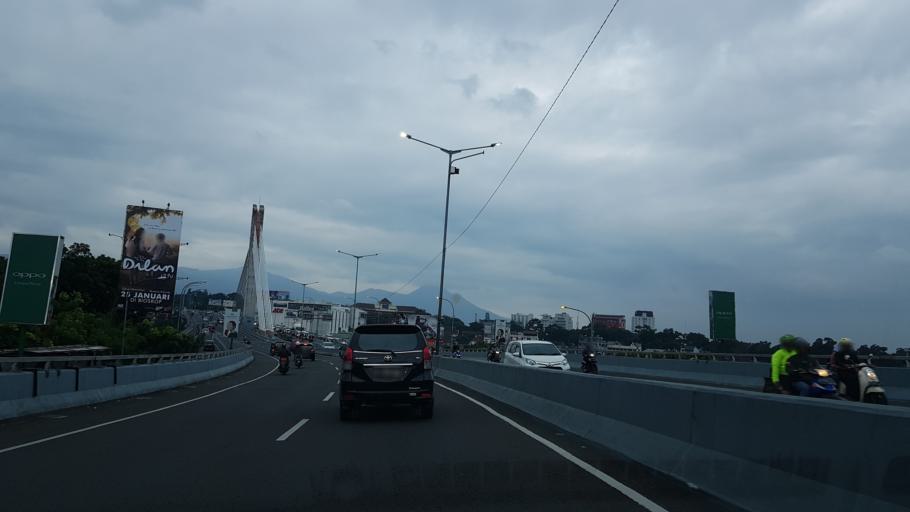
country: ID
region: West Java
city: Bandung
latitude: -6.9003
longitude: 107.6040
